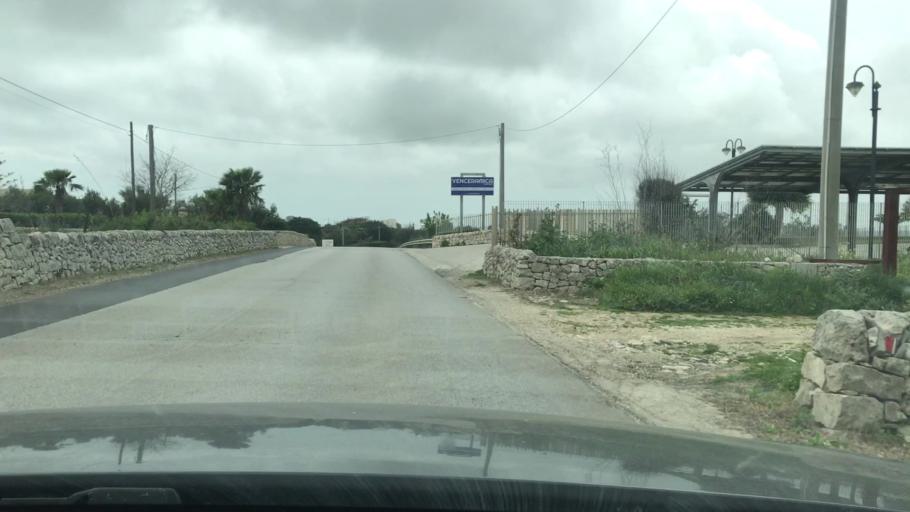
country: IT
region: Sicily
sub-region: Ragusa
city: Modica
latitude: 36.8202
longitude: 14.7454
